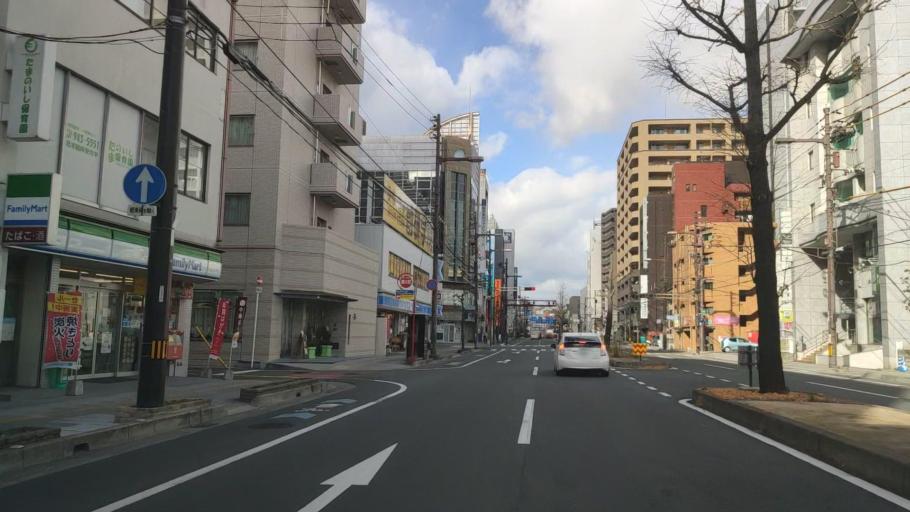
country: JP
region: Ehime
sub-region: Shikoku-chuo Shi
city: Matsuyama
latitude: 33.8393
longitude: 132.7753
